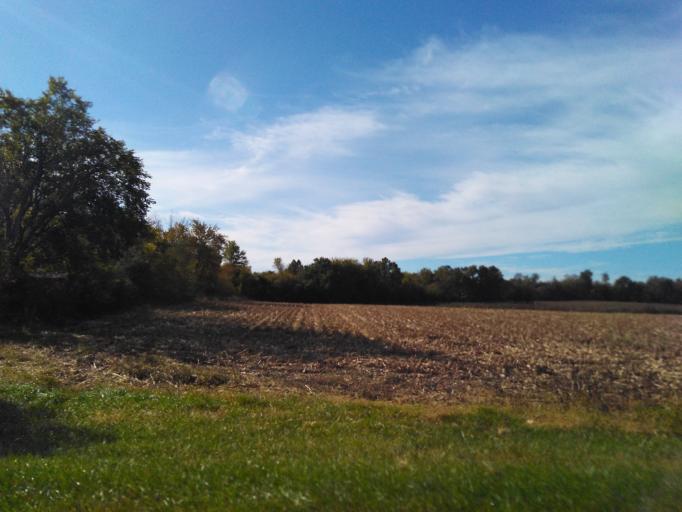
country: US
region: Illinois
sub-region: Madison County
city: Troy
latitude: 38.7172
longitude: -89.8384
